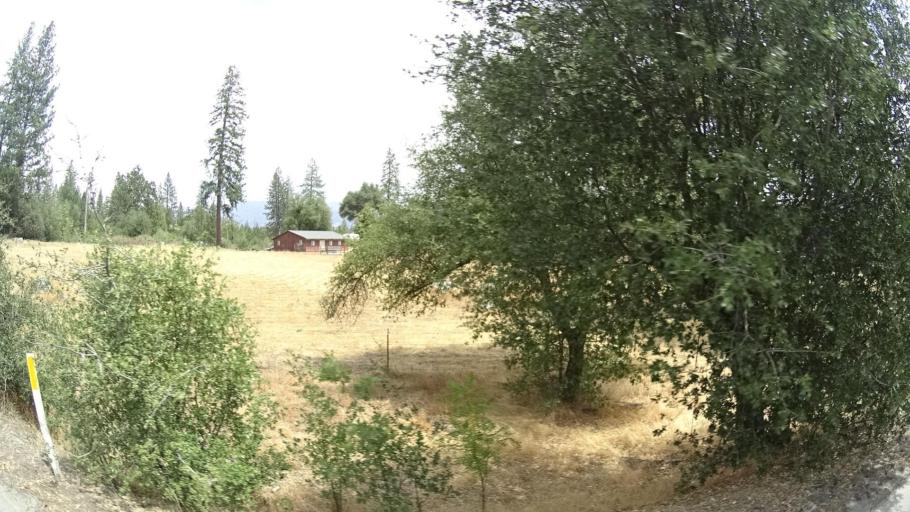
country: US
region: California
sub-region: Madera County
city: Ahwahnee
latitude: 37.4415
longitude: -119.8254
